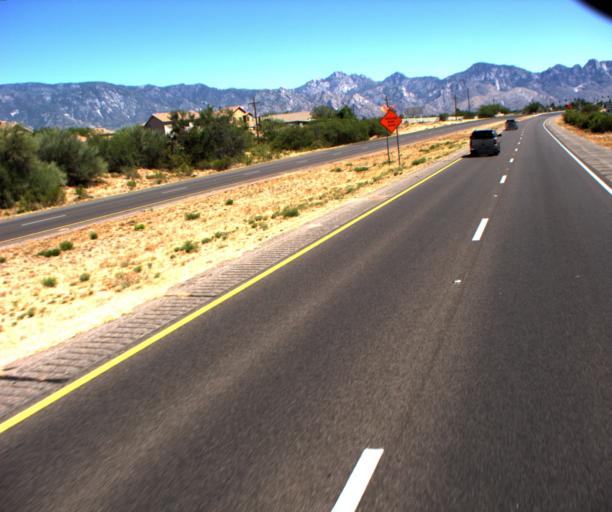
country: US
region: Arizona
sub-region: Pima County
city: Catalina
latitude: 32.5153
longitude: -110.9263
